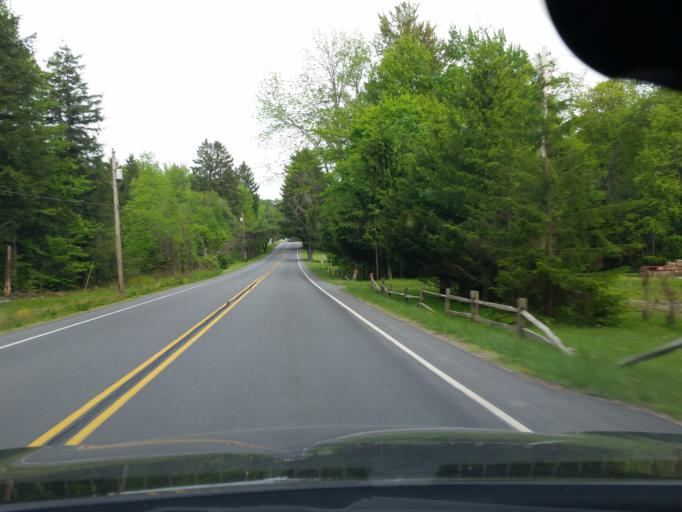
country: US
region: Pennsylvania
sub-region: McKean County
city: Kane
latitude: 41.5728
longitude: -78.9125
